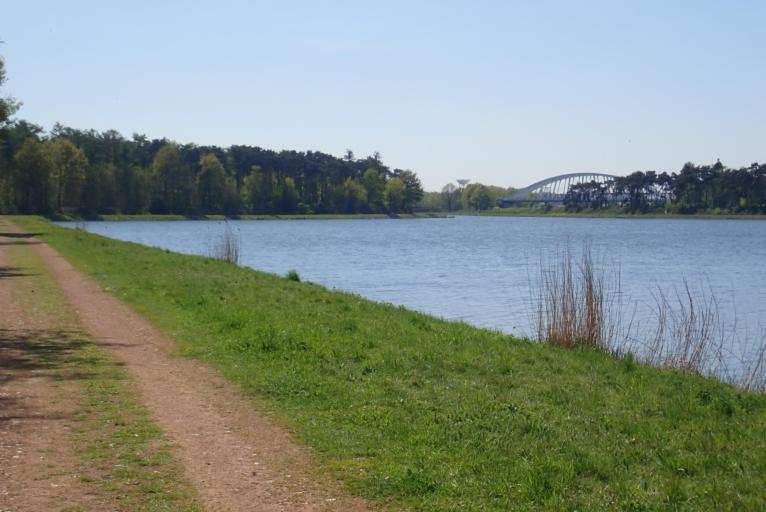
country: BE
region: Flanders
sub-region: Provincie Antwerpen
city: Duffel
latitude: 51.0899
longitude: 4.5076
